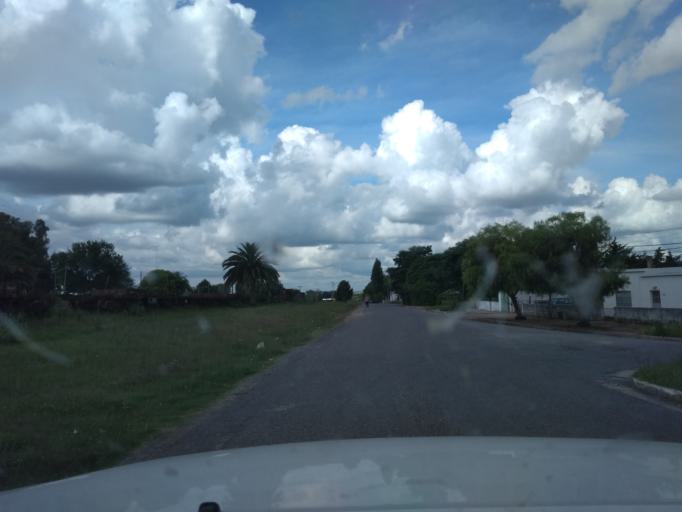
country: UY
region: Florida
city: Florida
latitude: -34.0875
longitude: -56.2136
